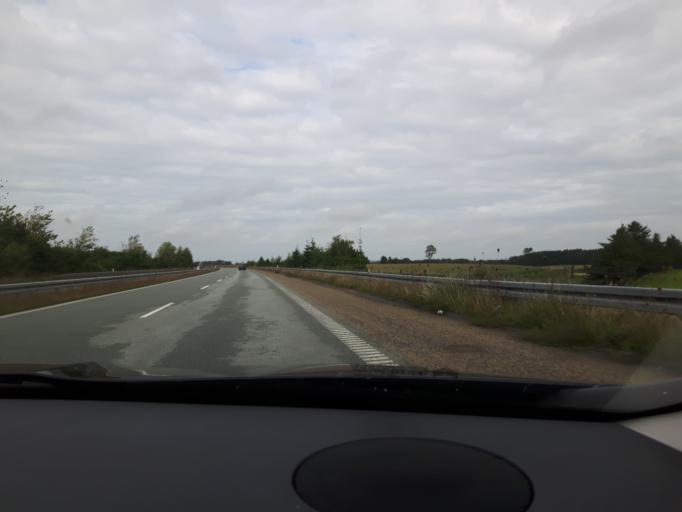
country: DK
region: North Denmark
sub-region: Hjorring Kommune
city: Hjorring
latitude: 57.4874
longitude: 10.0292
